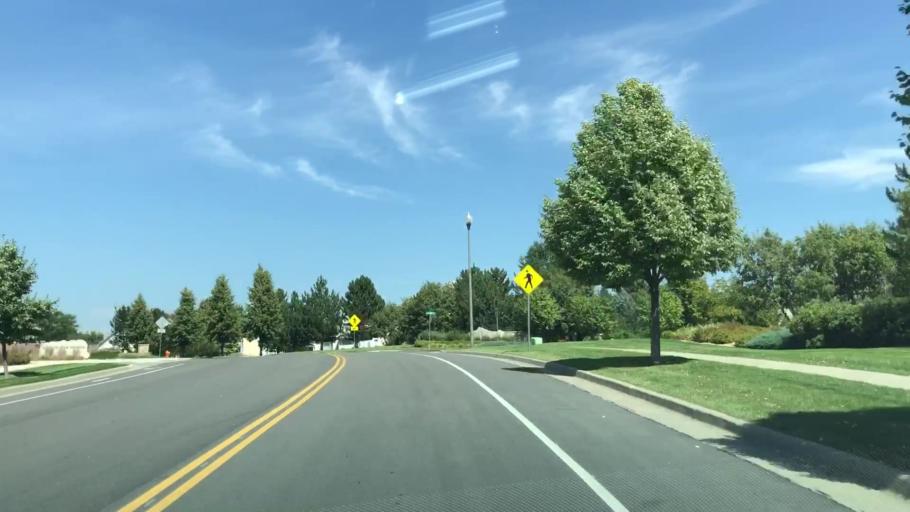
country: US
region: Colorado
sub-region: Larimer County
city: Loveland
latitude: 40.3939
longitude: -105.1407
